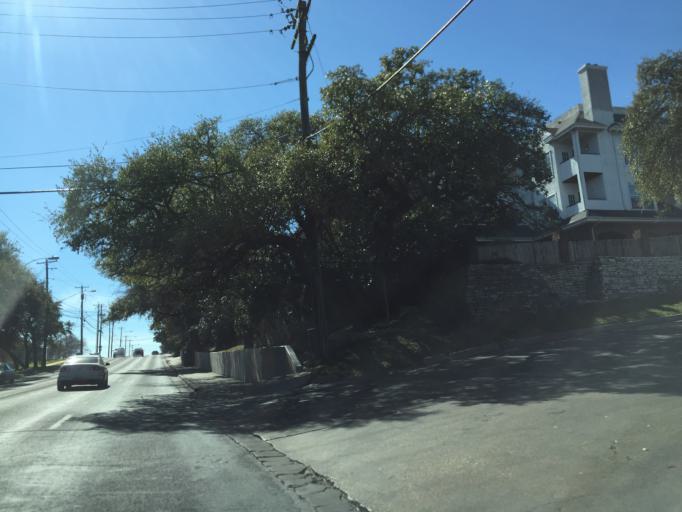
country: US
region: Texas
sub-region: Travis County
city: Austin
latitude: 30.2563
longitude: -97.7514
